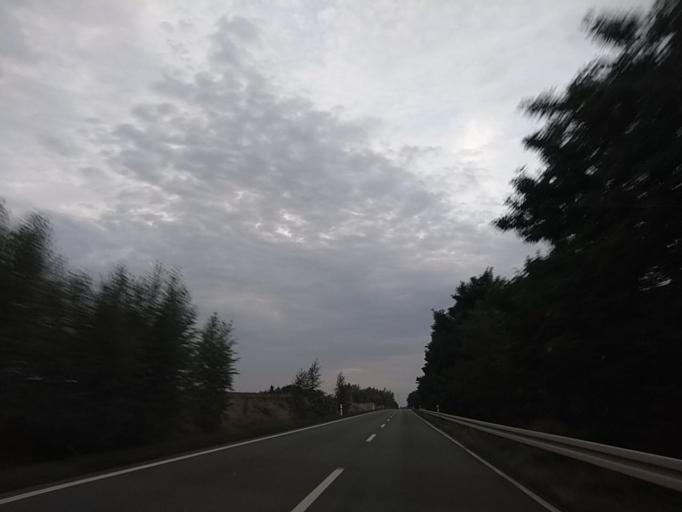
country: DE
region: Saxony-Anhalt
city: Theissen
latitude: 51.1108
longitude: 12.1441
